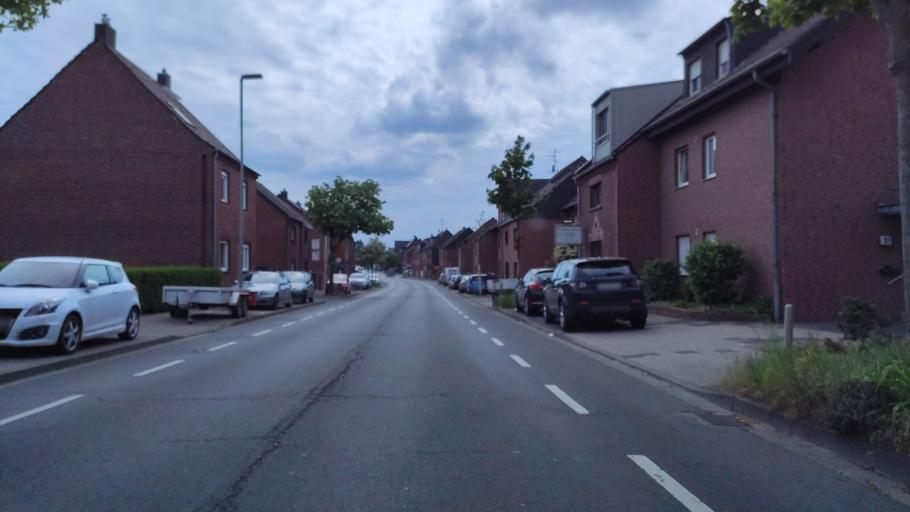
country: DE
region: North Rhine-Westphalia
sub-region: Regierungsbezirk Dusseldorf
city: Neuss
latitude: 51.1620
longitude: 6.6760
